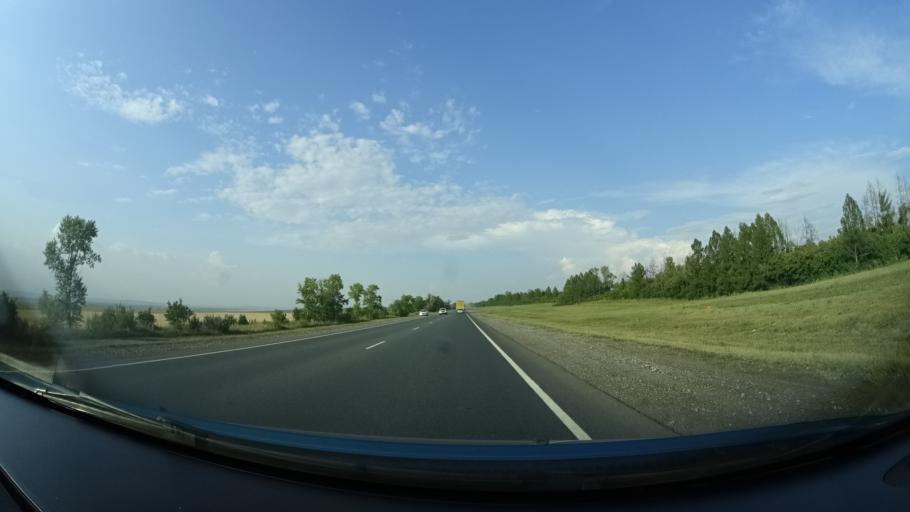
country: RU
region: Samara
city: Krasnyy Yar
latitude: 53.6414
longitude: 50.7308
